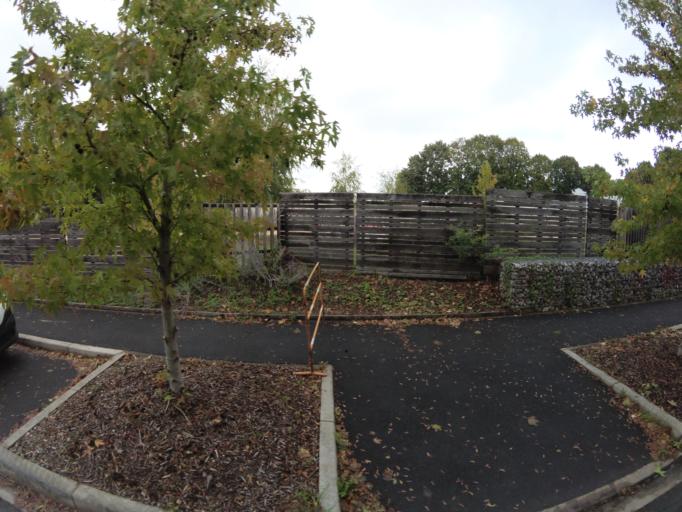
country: FR
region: Ile-de-France
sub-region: Departement de Seine-et-Marne
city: Bussy-Saint-Georges
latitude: 48.8421
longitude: 2.7006
